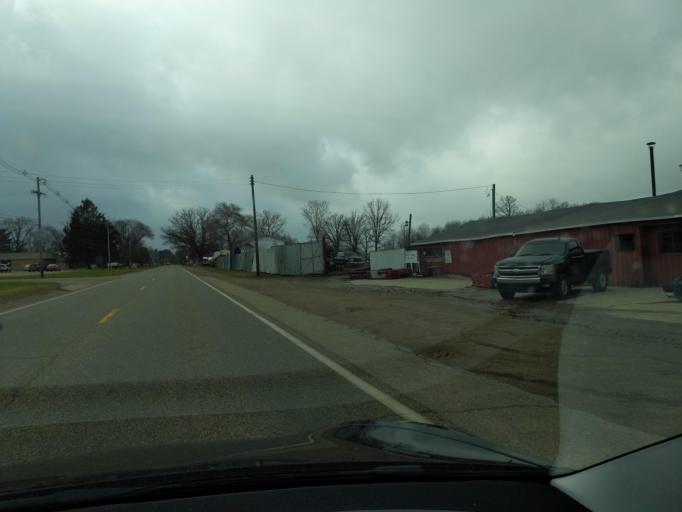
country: US
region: Michigan
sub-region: Jackson County
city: Spring Arbor
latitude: 42.2530
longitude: -84.5126
